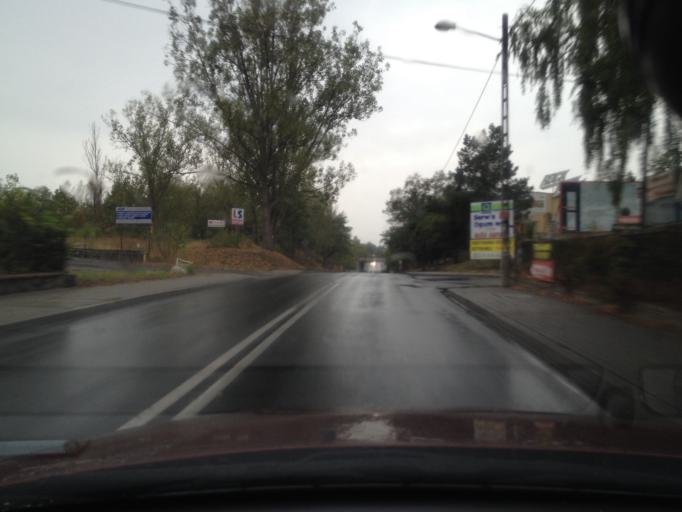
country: PL
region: Lubusz
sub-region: Powiat zaganski
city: Zagan
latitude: 51.6101
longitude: 15.3025
